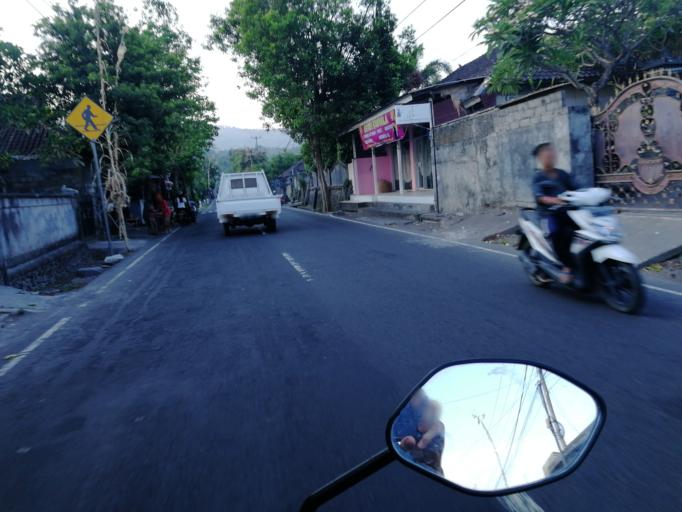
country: ID
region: Bali
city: Banjar Buayang
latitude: -8.3475
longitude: 115.6149
